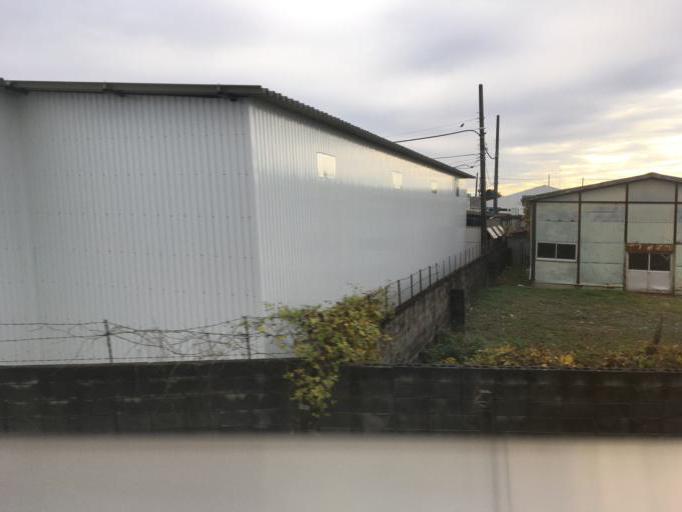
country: JP
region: Tochigi
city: Tochigi
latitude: 36.3655
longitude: 139.7543
